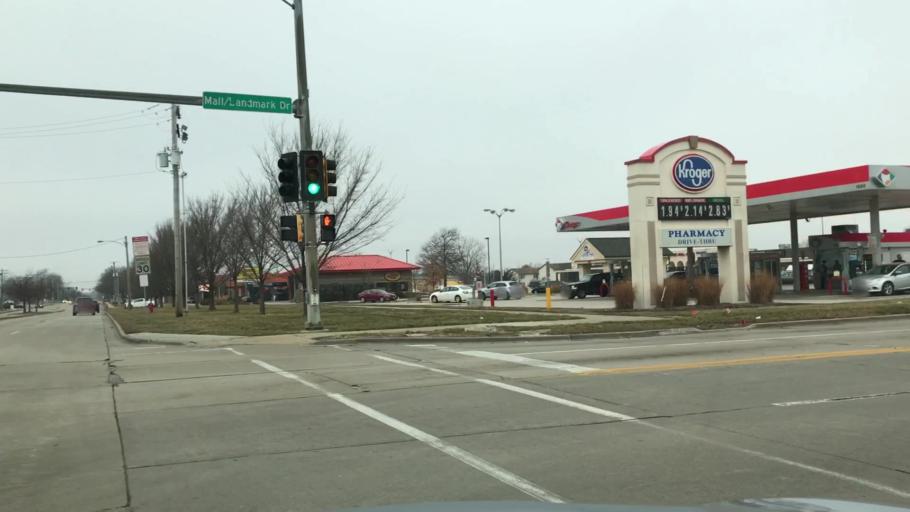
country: US
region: Illinois
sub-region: McLean County
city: Normal
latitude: 40.5105
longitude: -88.9553
